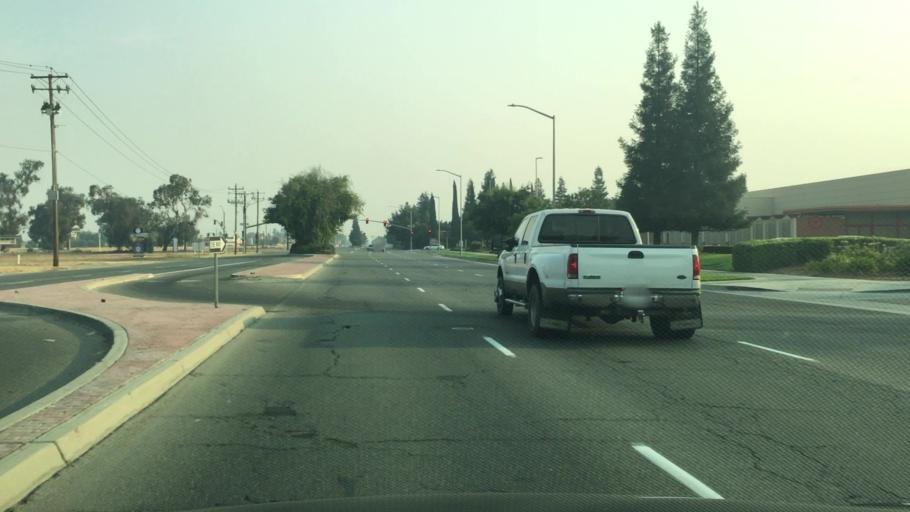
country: US
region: California
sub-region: Fresno County
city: Clovis
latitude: 36.8393
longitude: -119.7296
